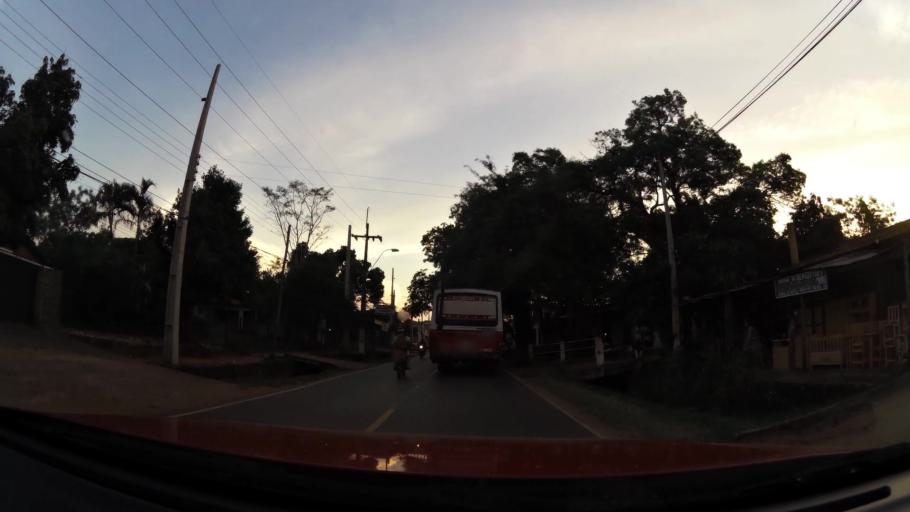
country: PY
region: Central
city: Nemby
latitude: -25.3827
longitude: -57.4950
